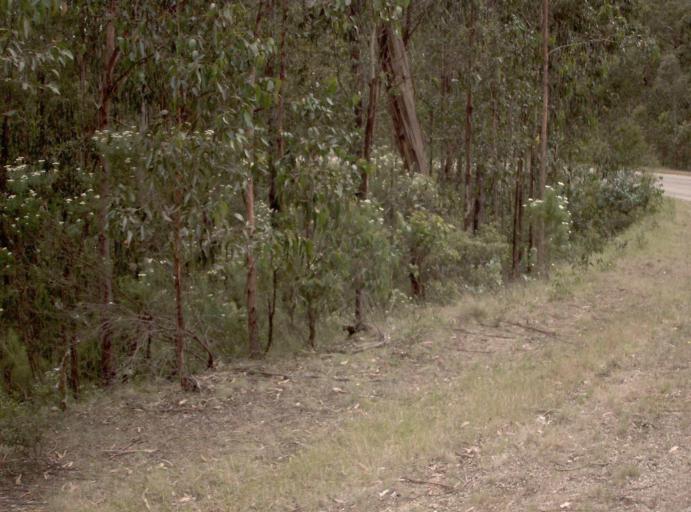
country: AU
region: Victoria
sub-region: East Gippsland
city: Bairnsdale
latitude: -37.6015
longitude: 147.1929
